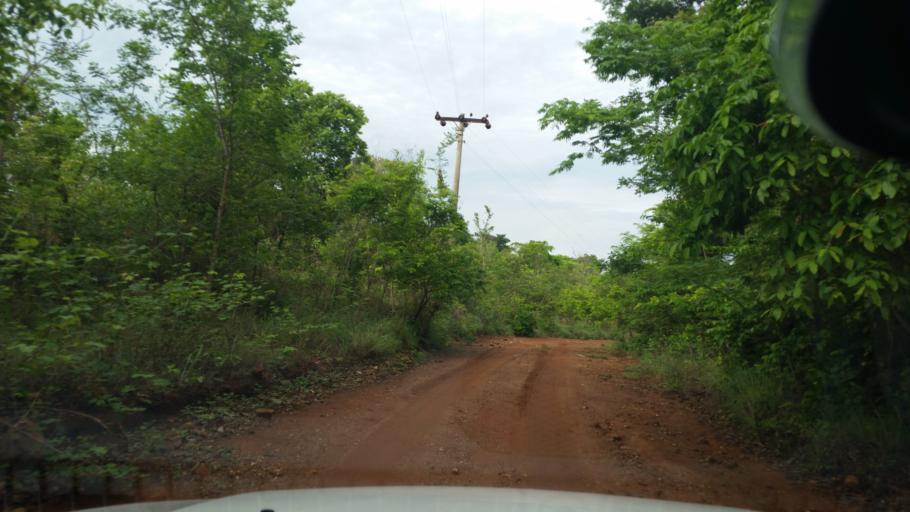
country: BR
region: Goias
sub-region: Porangatu
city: Porangatu
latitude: -13.9801
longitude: -49.2709
